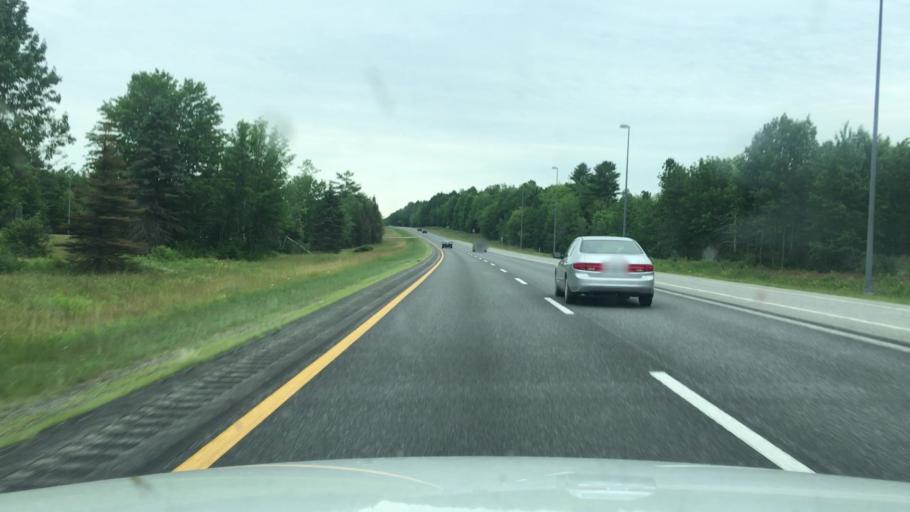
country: US
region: Maine
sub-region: Sagadahoc County
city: Richmond
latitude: 44.0954
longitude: -69.8732
